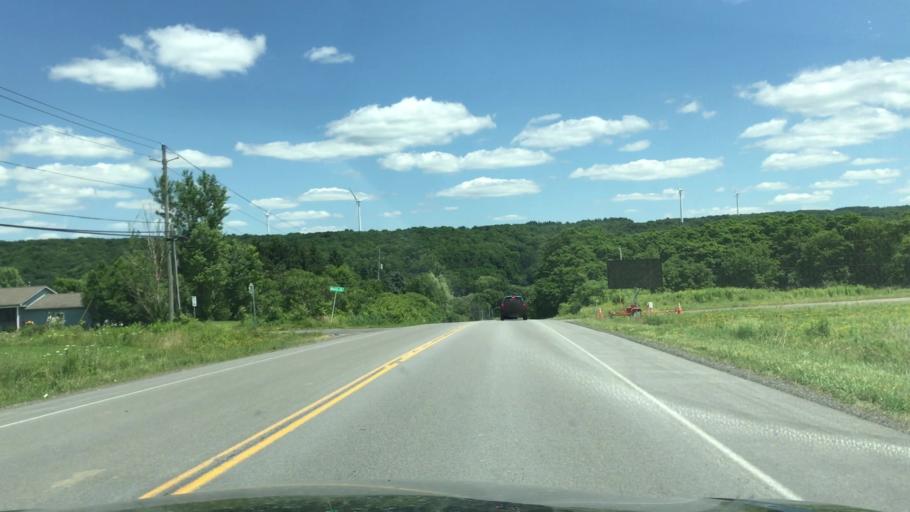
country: US
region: New York
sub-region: Wyoming County
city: Attica
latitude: 42.7704
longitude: -78.3835
